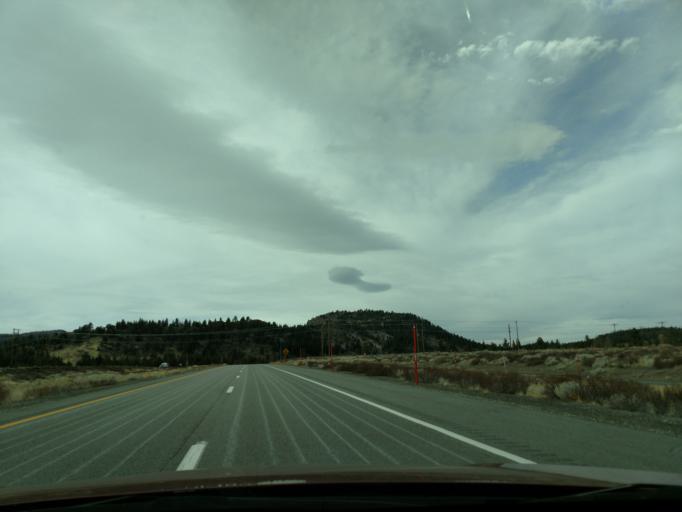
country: US
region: California
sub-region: Mono County
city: Mammoth Lakes
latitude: 37.6421
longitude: -118.9177
